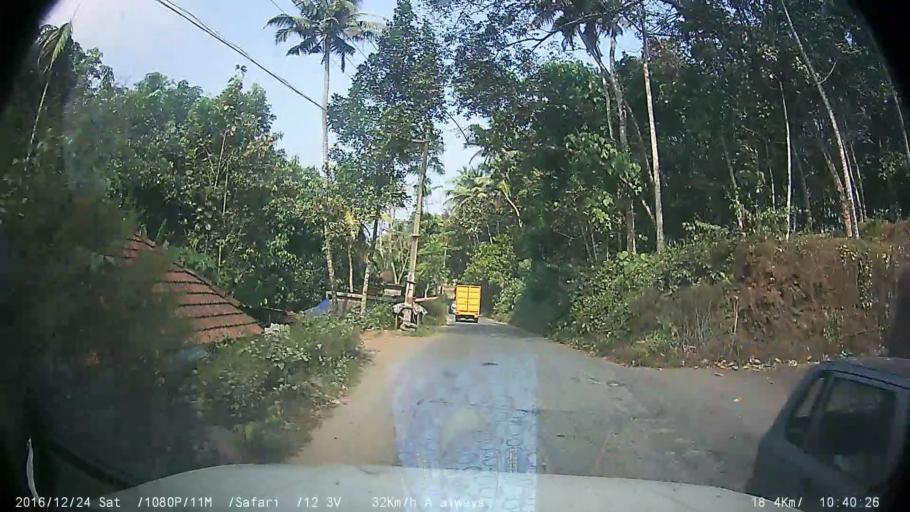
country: IN
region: Kerala
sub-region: Ernakulam
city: Piravam
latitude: 9.8714
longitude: 76.6074
